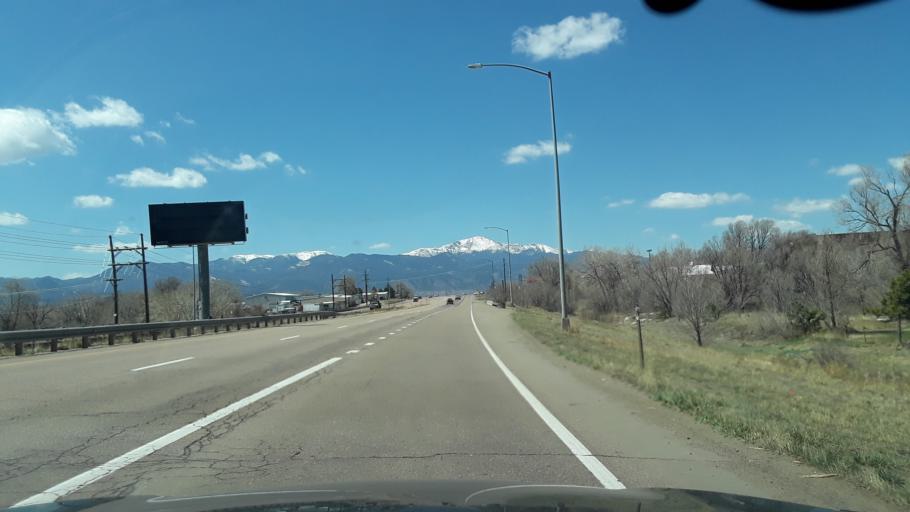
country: US
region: Colorado
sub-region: El Paso County
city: Cimarron Hills
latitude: 38.8392
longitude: -104.7049
